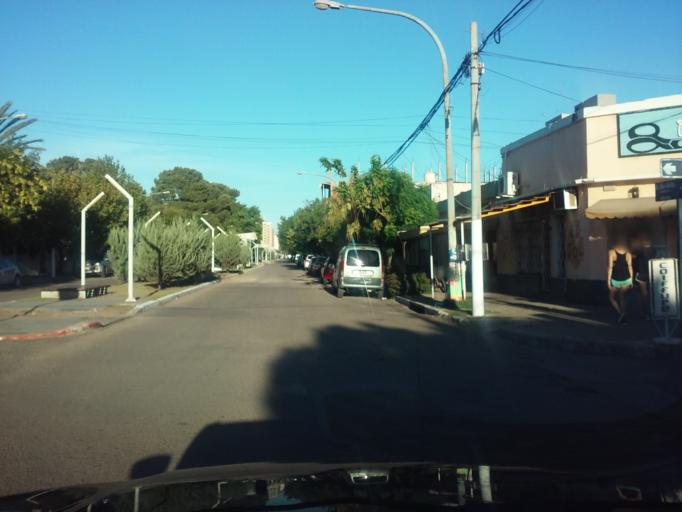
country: AR
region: La Pampa
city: Santa Rosa
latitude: -36.6210
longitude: -64.2977
